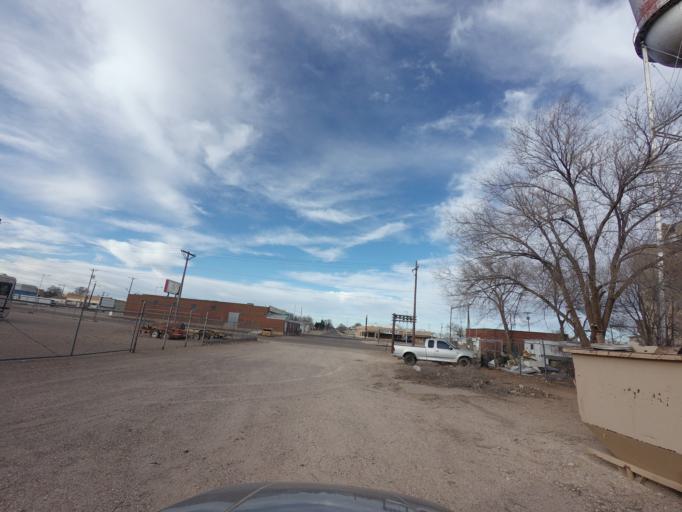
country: US
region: New Mexico
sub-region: Curry County
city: Clovis
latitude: 34.3978
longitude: -103.2015
